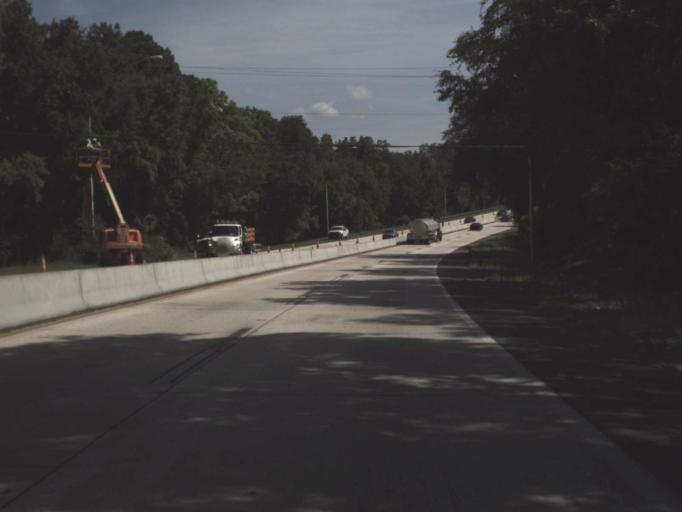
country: US
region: Florida
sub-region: Duval County
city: Jacksonville
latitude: 30.3160
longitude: -81.7038
